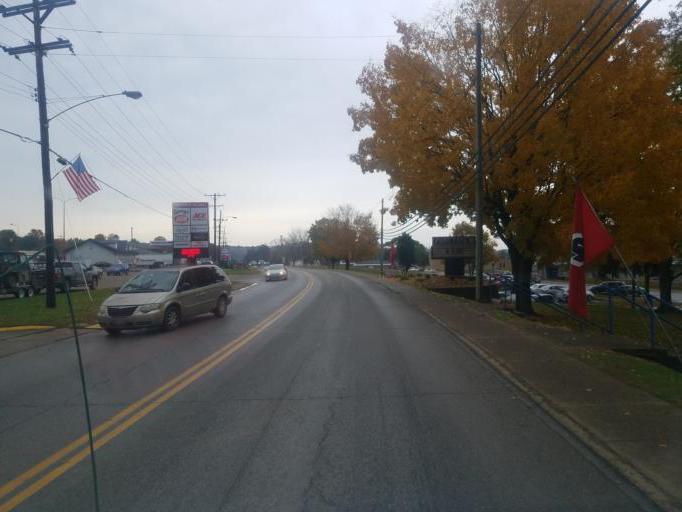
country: US
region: Ohio
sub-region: Washington County
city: Beverly
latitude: 39.5482
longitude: -81.6326
